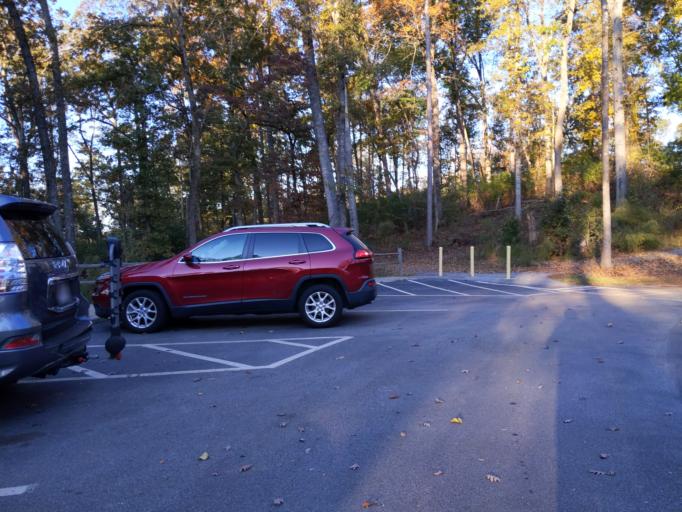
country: US
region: Georgia
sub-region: Franklin County
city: Gumlog
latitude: 34.4925
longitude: -83.0706
